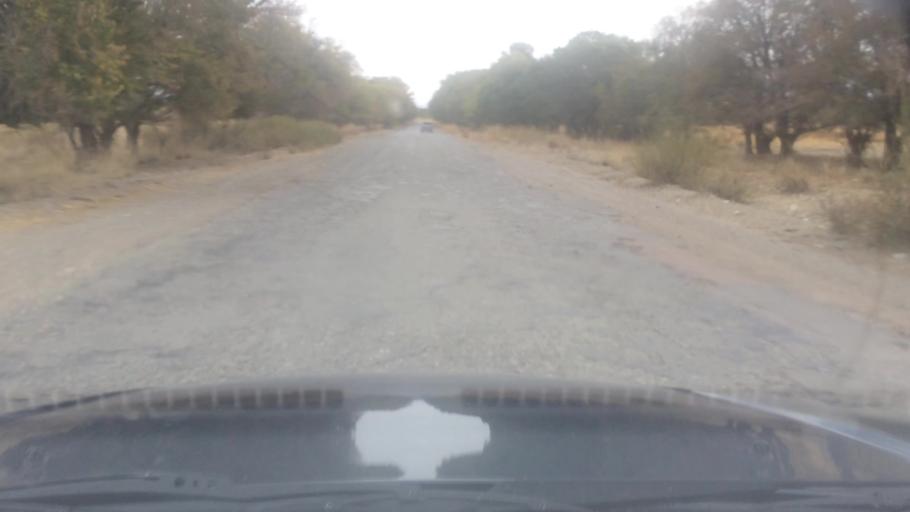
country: KG
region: Ysyk-Koel
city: Balykchy
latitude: 42.3100
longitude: 76.4603
